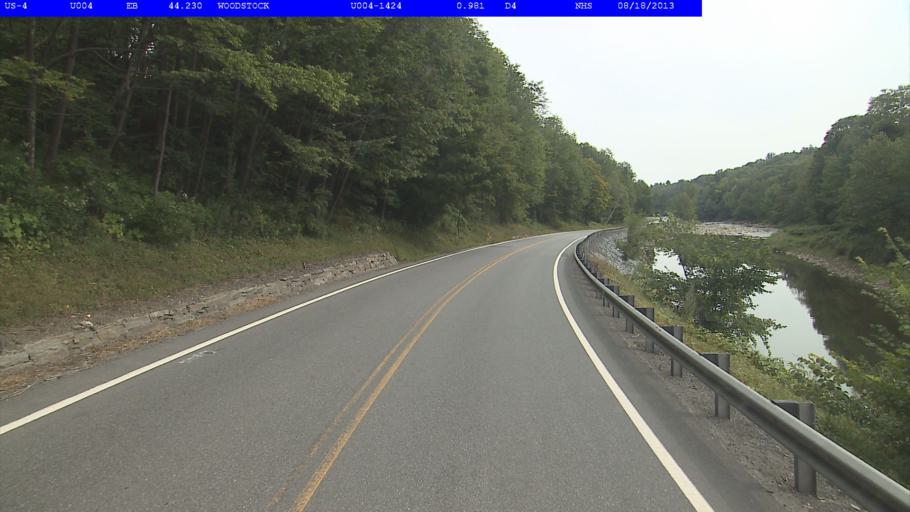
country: US
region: Vermont
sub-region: Windsor County
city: Woodstock
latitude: 43.5943
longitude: -72.6069
